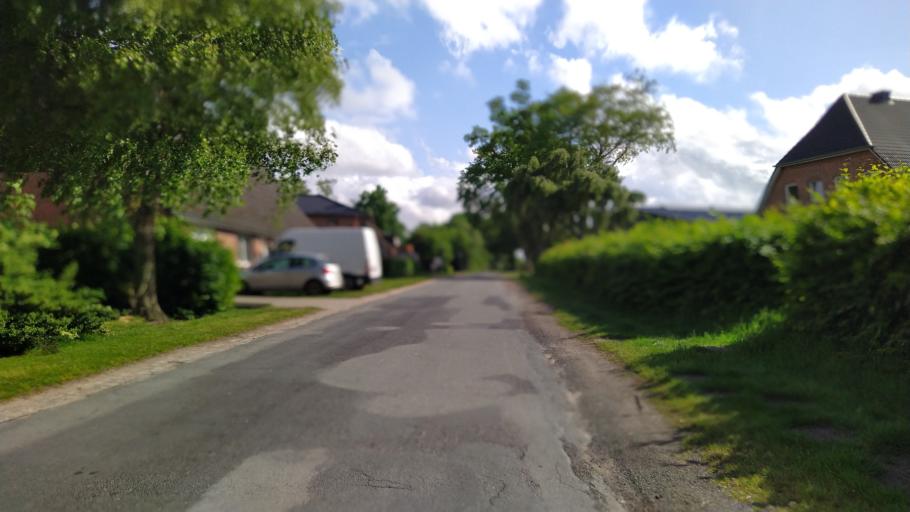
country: DE
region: Lower Saxony
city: Brest
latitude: 53.4503
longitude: 9.3827
